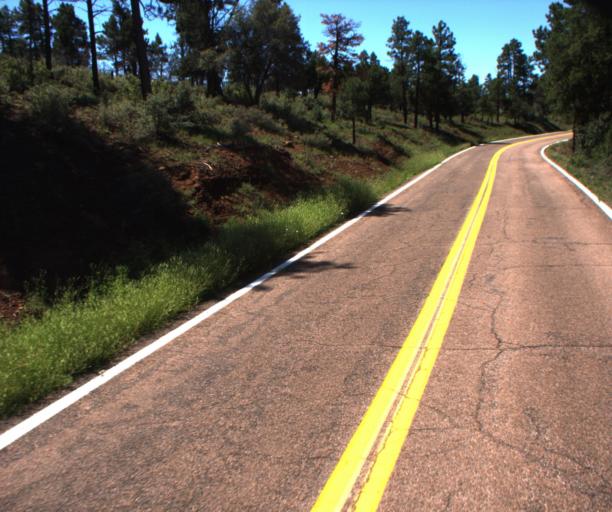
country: US
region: Arizona
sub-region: Greenlee County
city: Morenci
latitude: 33.5170
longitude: -109.3088
